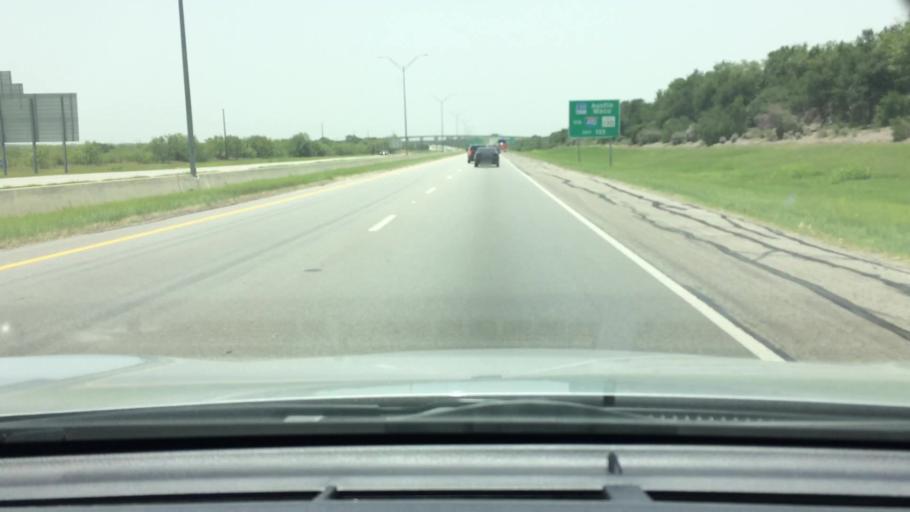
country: US
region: Texas
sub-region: Bexar County
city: China Grove
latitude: 29.3401
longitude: -98.4211
